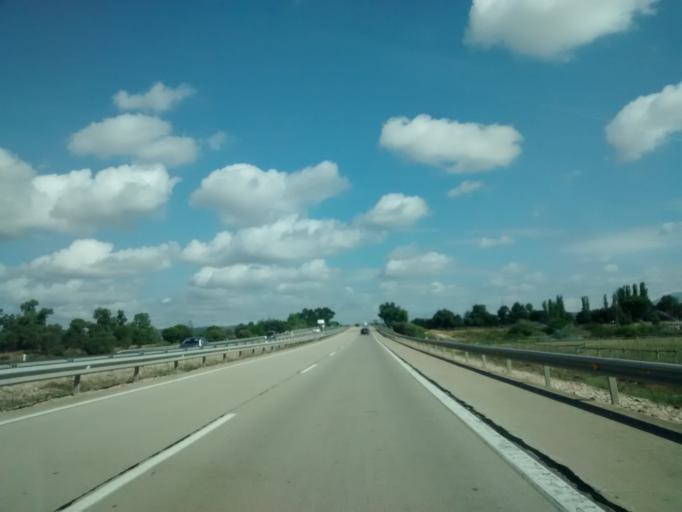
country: ES
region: Castille-La Mancha
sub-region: Province of Toledo
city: Talavera de la Reina
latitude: 39.9925
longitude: -4.7608
